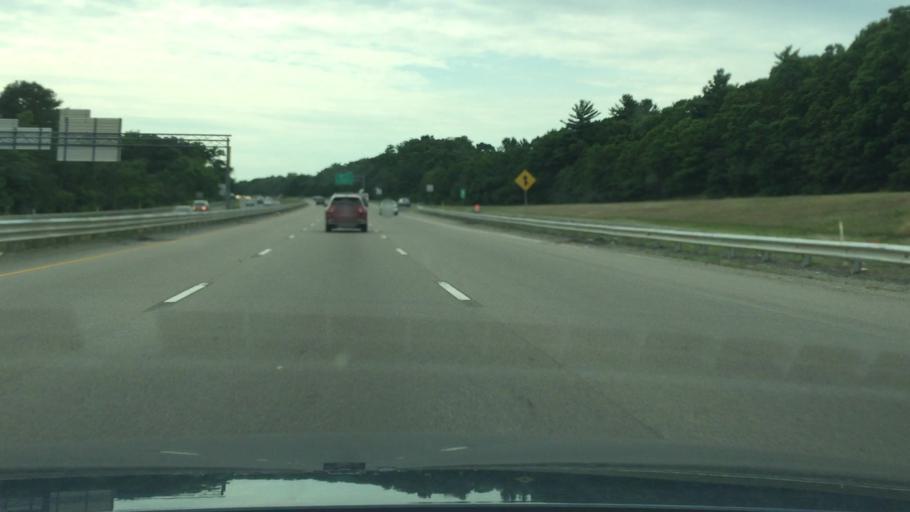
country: US
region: Massachusetts
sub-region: Plymouth County
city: North Plymouth
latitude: 41.9563
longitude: -70.6840
